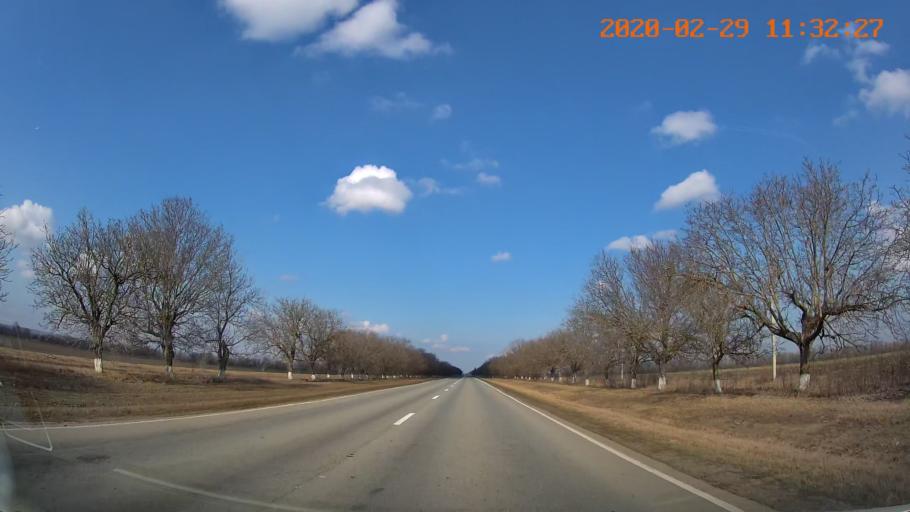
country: MD
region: Rezina
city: Saharna
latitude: 47.5383
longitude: 29.0942
